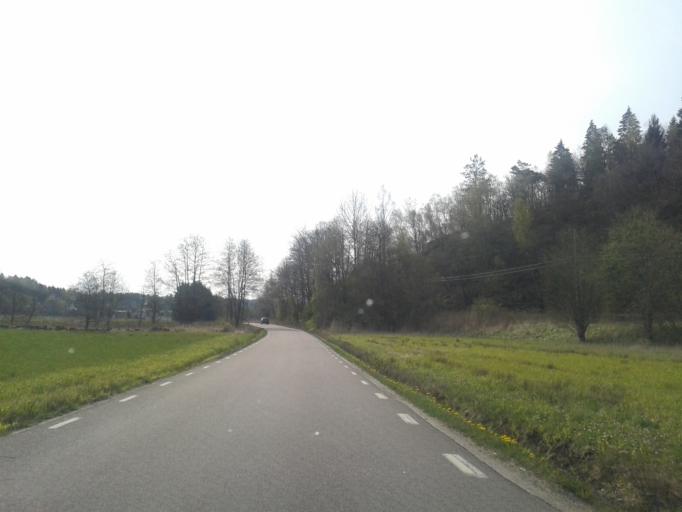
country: SE
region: Vaestra Goetaland
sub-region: Kungalvs Kommun
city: Kode
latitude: 57.9069
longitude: 11.8935
